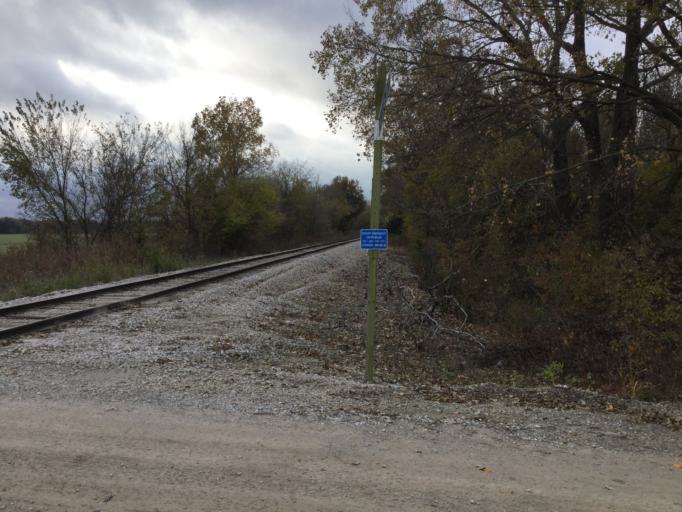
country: US
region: Kansas
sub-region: Montgomery County
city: Coffeyville
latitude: 37.1374
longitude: -95.5978
